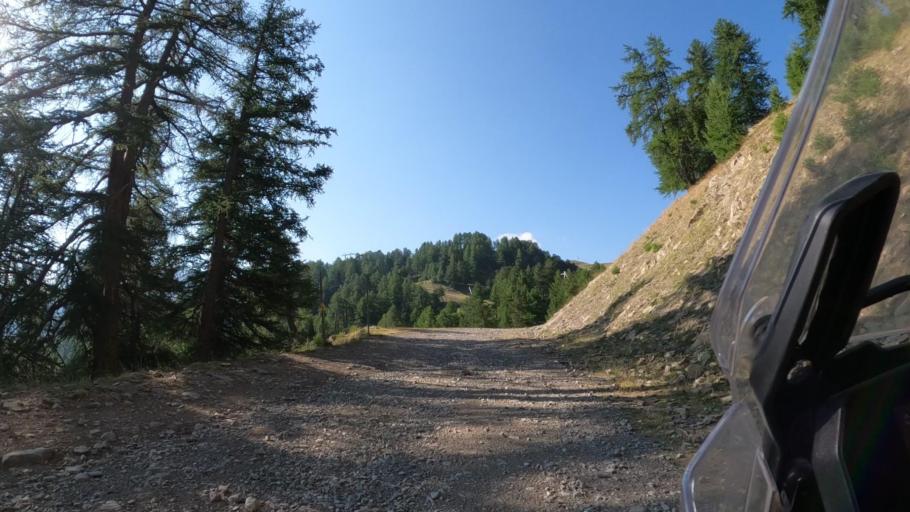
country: FR
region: Provence-Alpes-Cote d'Azur
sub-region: Departement des Hautes-Alpes
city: Guillestre
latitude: 44.6111
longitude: 6.6246
